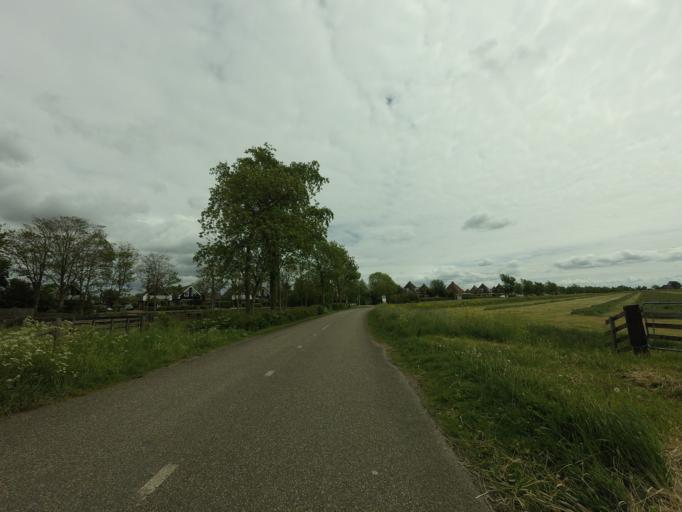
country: NL
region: Friesland
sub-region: Sudwest Fryslan
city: Woudsend
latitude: 52.9499
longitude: 5.6194
